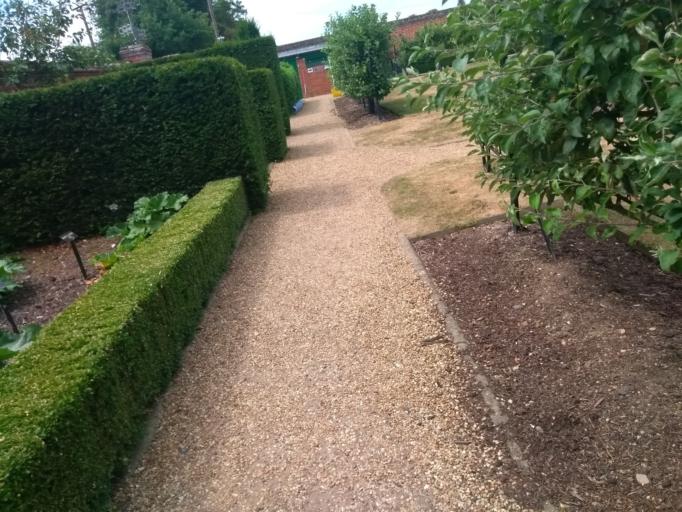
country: GB
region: England
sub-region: Essex
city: Saffron Walden
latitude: 52.0266
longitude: 0.2366
